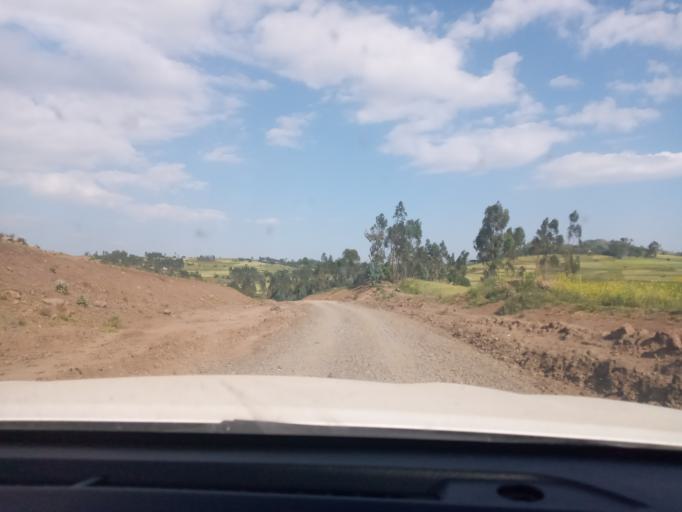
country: ET
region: Amhara
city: Were Ilu
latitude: 10.6141
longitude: 39.0429
